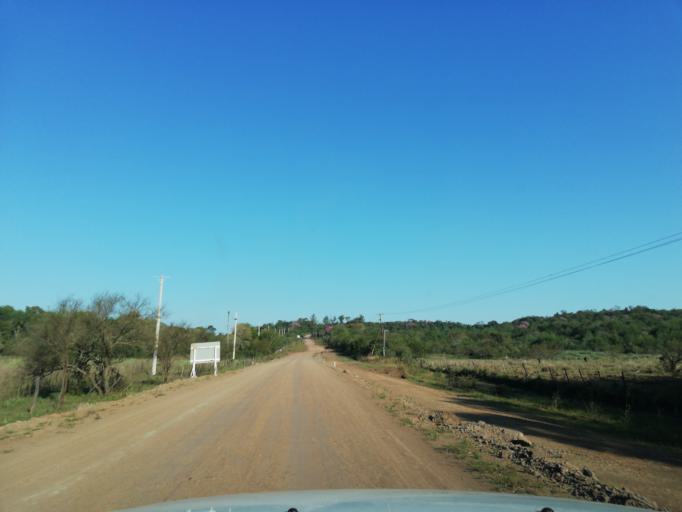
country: AR
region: Misiones
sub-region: Departamento de Candelaria
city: Candelaria
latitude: -27.5358
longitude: -55.7167
